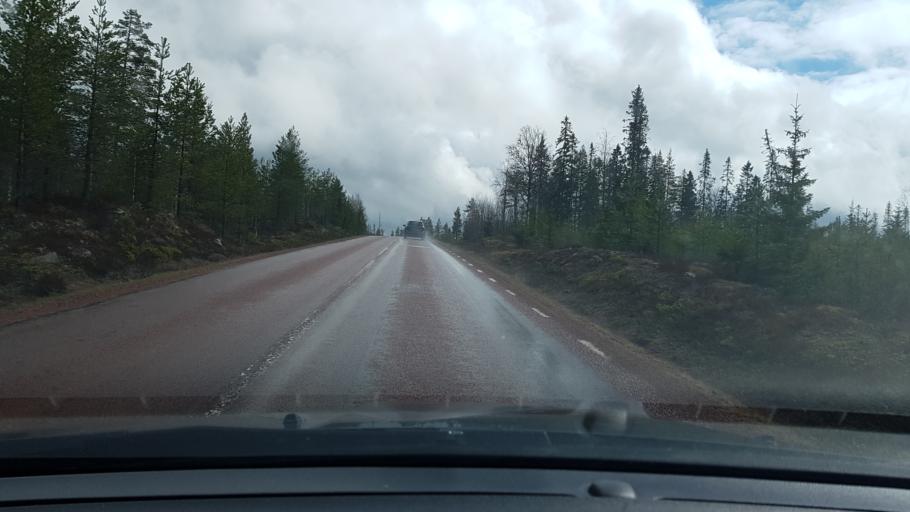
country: SE
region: Dalarna
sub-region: Malung-Saelens kommun
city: Malung
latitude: 61.0504
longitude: 13.3662
